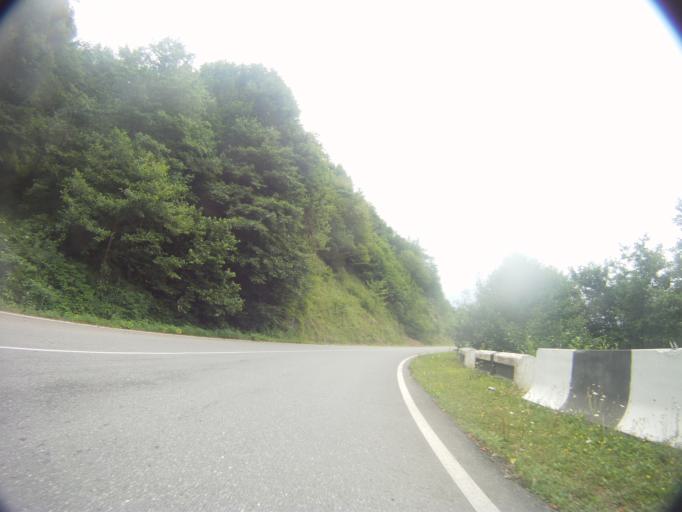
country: GE
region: Samegrelo and Zemo Svaneti
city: Jvari
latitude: 42.8168
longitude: 42.0316
